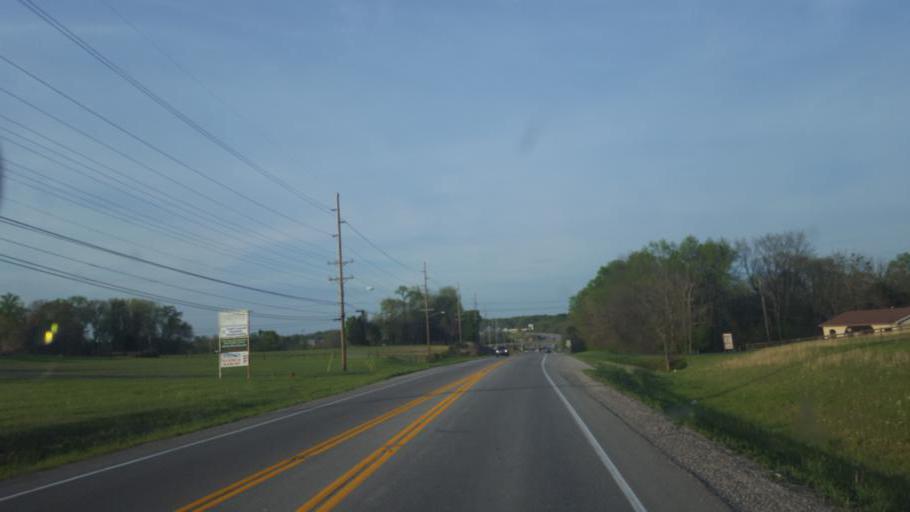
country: US
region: Kentucky
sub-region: Barren County
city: Glasgow
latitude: 36.9732
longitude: -85.9395
